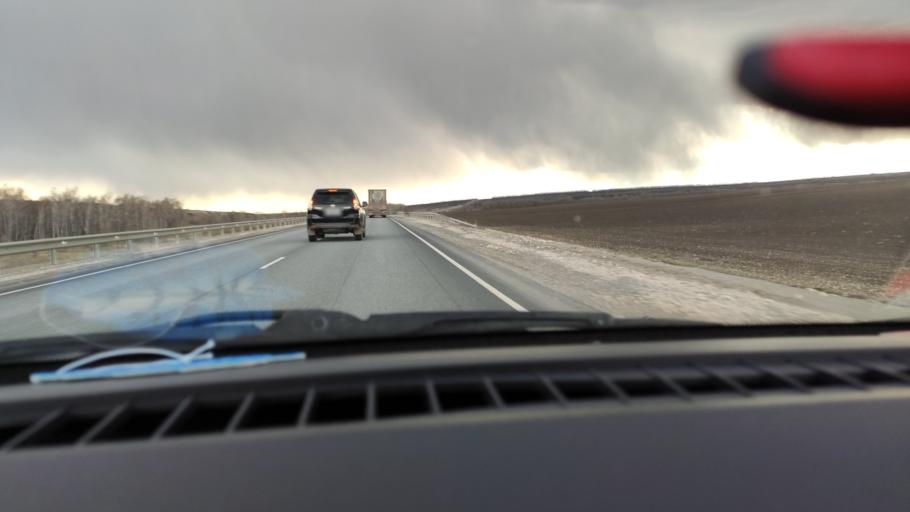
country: RU
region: Saratov
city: Yelshanka
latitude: 51.8576
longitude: 46.4959
